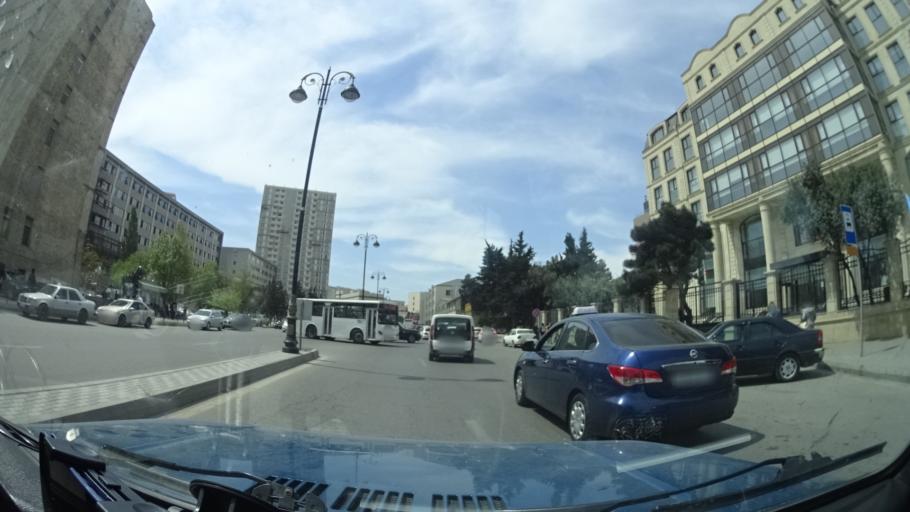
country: AZ
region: Baki
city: Khodzhi-Gasan
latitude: 40.4032
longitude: 49.8069
